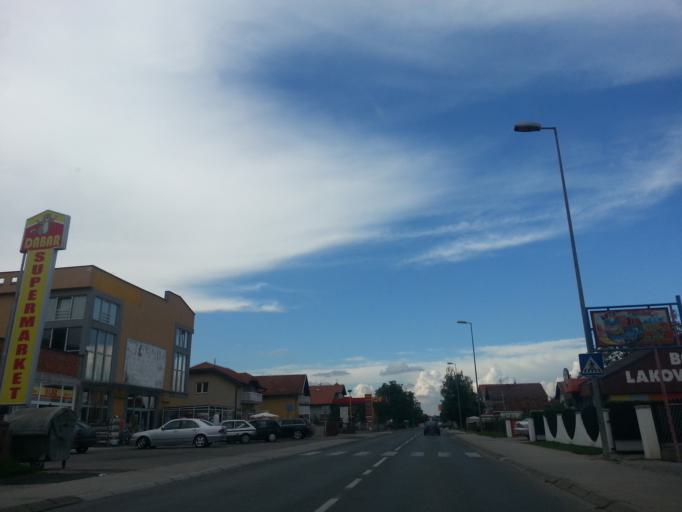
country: BA
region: Brcko
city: Brcko
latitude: 44.8578
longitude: 18.8130
